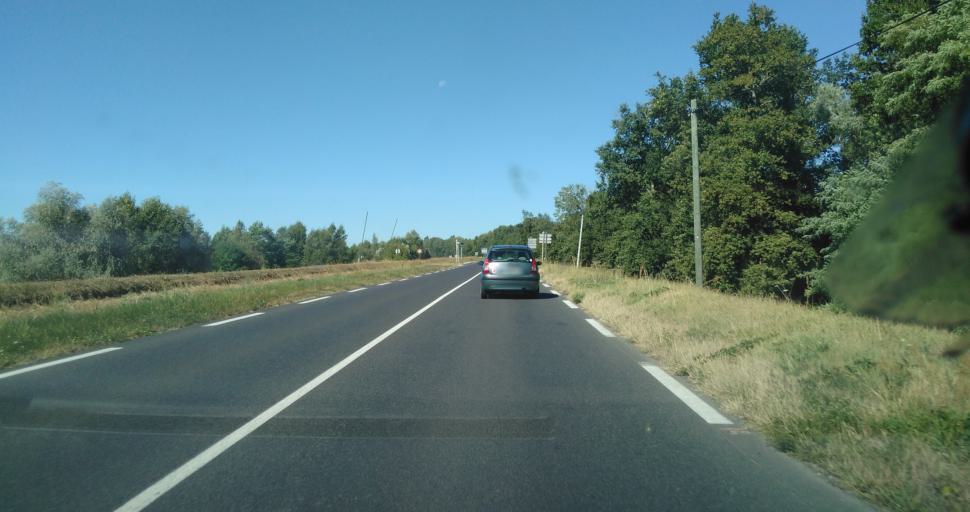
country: FR
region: Centre
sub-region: Departement d'Indre-et-Loire
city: Noizay
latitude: 47.4043
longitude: 0.8999
